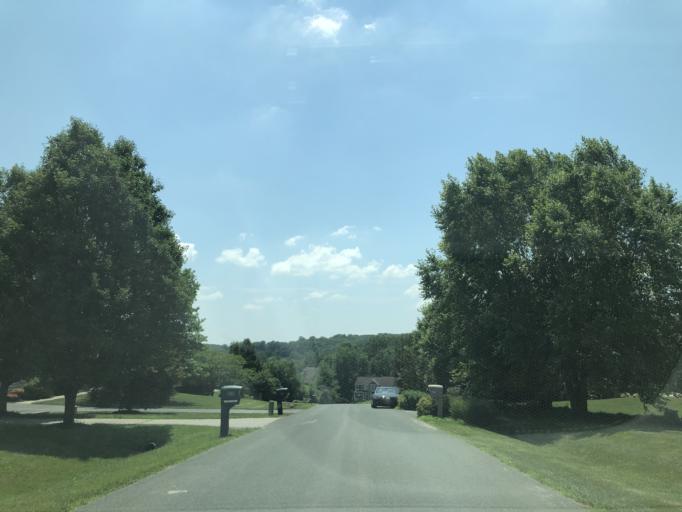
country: US
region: Maryland
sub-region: Carroll County
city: Westminster
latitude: 39.5229
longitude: -76.9522
